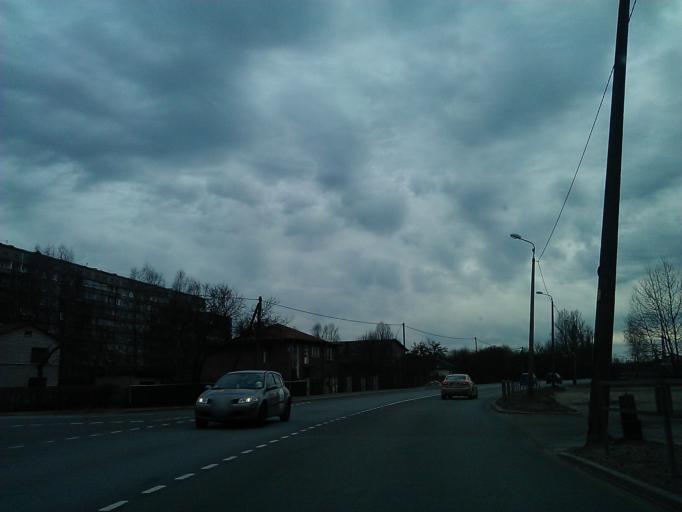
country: LV
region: Riga
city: Riga
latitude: 56.9563
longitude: 24.1656
